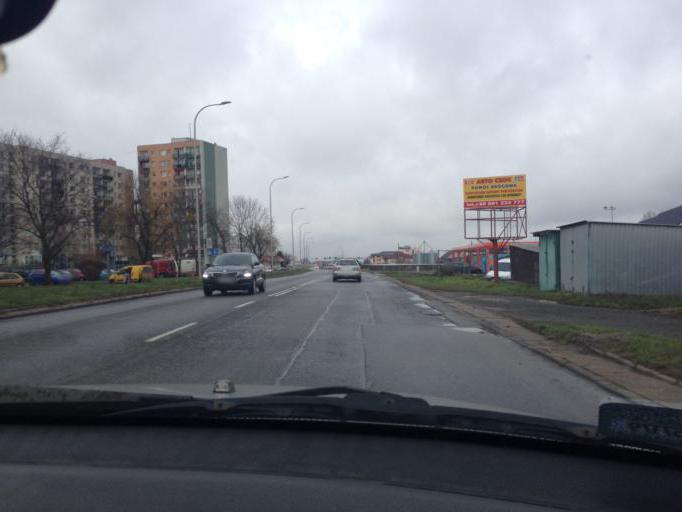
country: PL
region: Opole Voivodeship
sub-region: Powiat opolski
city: Opole
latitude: 50.6838
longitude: 17.9538
